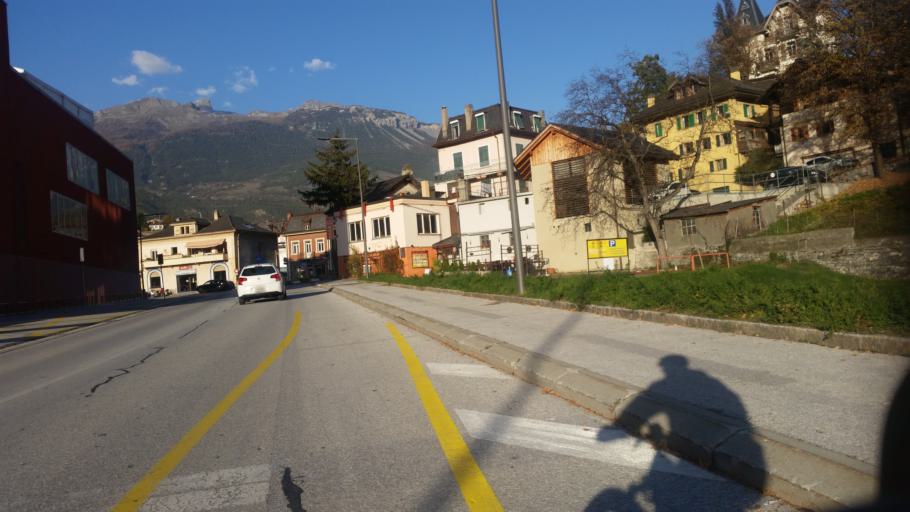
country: CH
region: Valais
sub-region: Sierre District
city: Sierre
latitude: 46.2928
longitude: 7.5370
